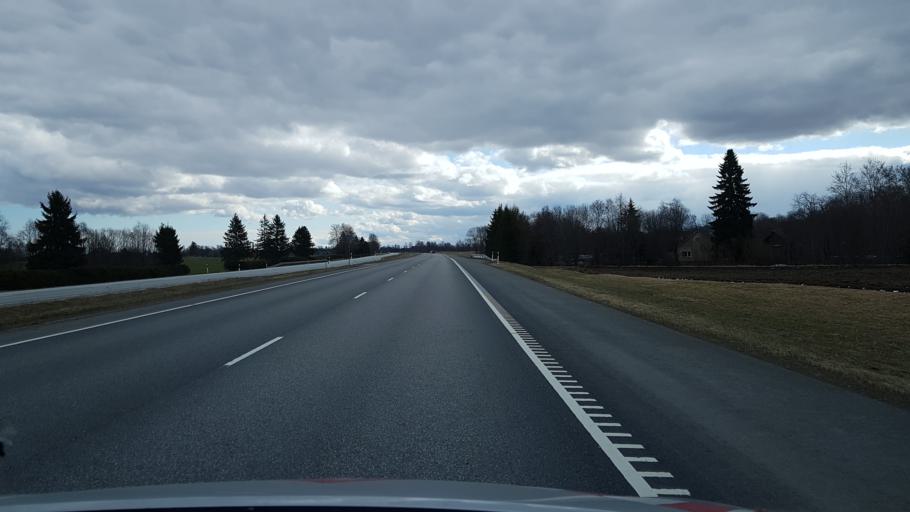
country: EE
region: Laeaene-Virumaa
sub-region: Kadrina vald
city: Kadrina
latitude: 59.4423
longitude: 26.1078
